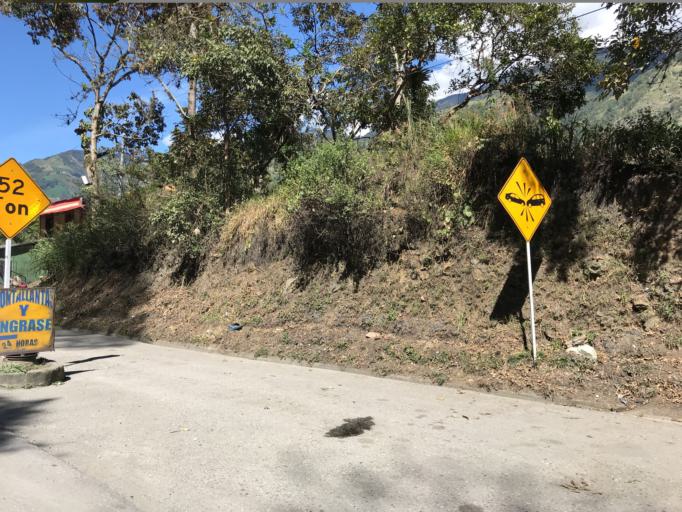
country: CO
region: Tolima
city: Cajamarca
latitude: 4.4420
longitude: -75.4185
